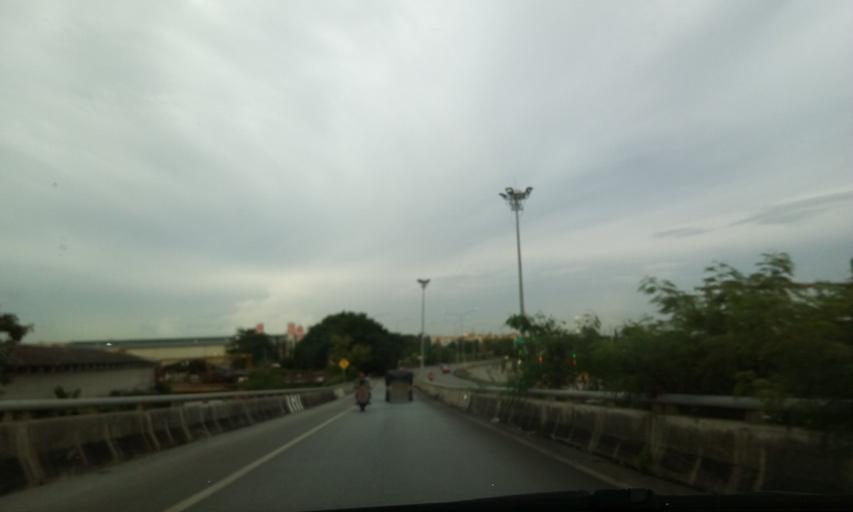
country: TH
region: Phra Nakhon Si Ayutthaya
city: Ban Bang Kadi Pathum Thani
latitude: 13.9728
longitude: 100.5514
